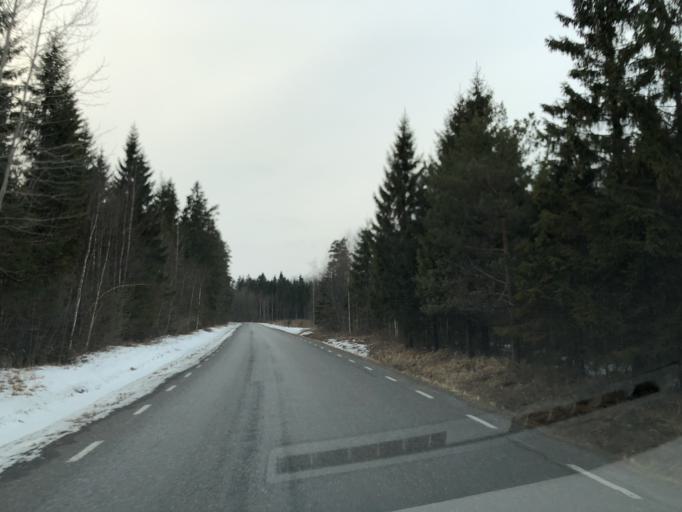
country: EE
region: Paernumaa
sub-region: Vaendra vald (alev)
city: Vandra
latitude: 58.6938
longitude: 24.9727
